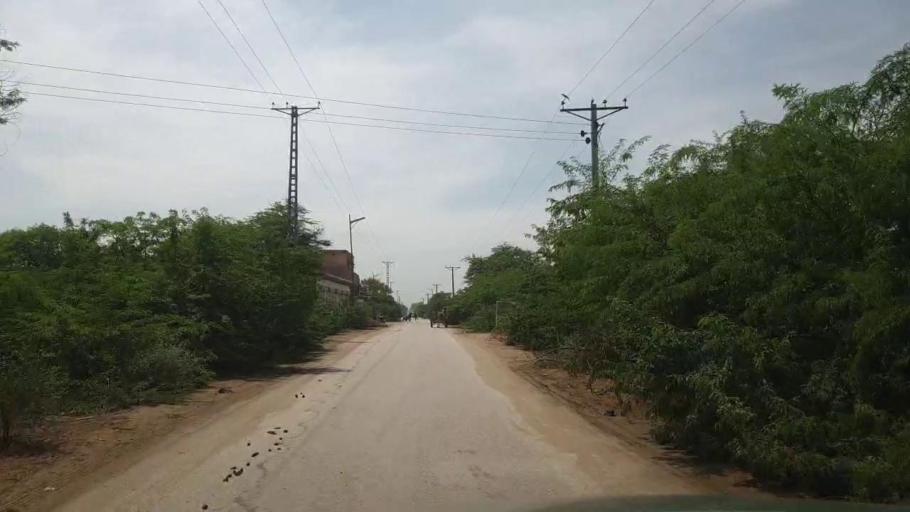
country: PK
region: Sindh
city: Kot Diji
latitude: 27.1617
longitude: 68.9562
